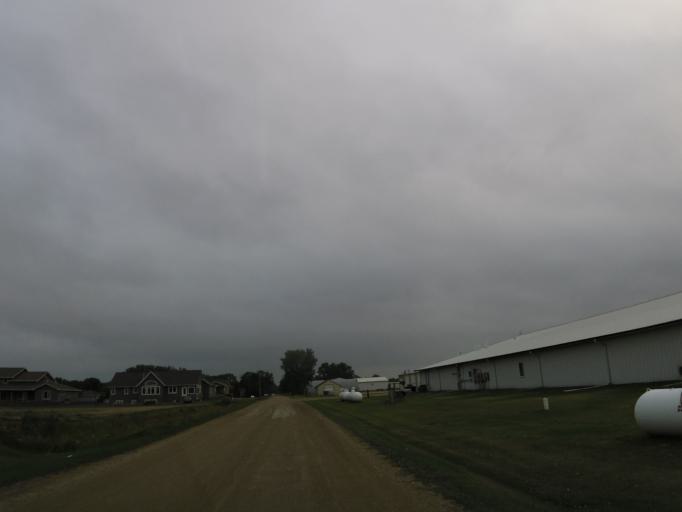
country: US
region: North Dakota
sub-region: Walsh County
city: Grafton
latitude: 48.5708
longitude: -97.1765
